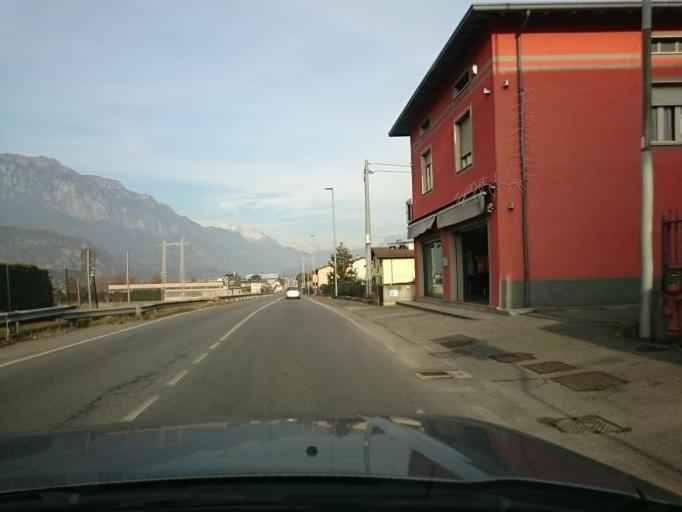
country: IT
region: Lombardy
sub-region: Provincia di Brescia
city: Artogne
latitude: 45.8539
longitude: 10.1540
